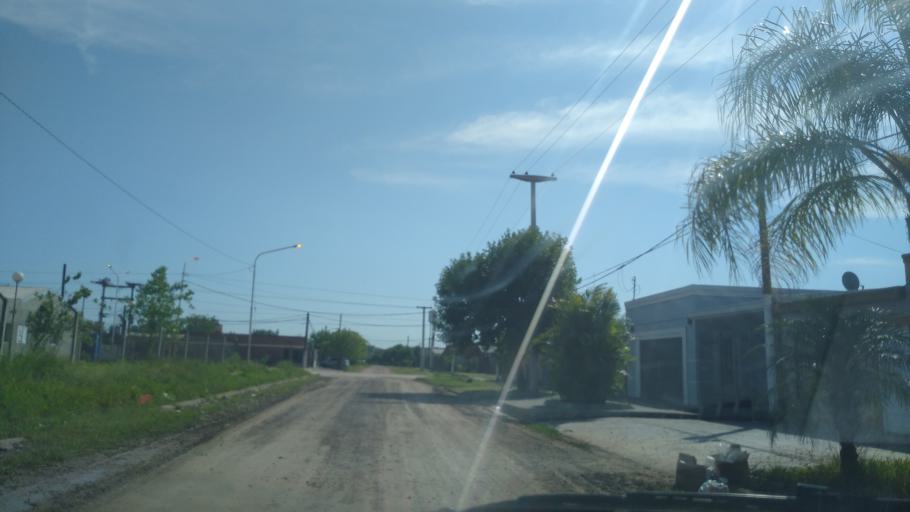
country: AR
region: Chaco
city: Barranqueras
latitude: -27.4943
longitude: -58.9599
